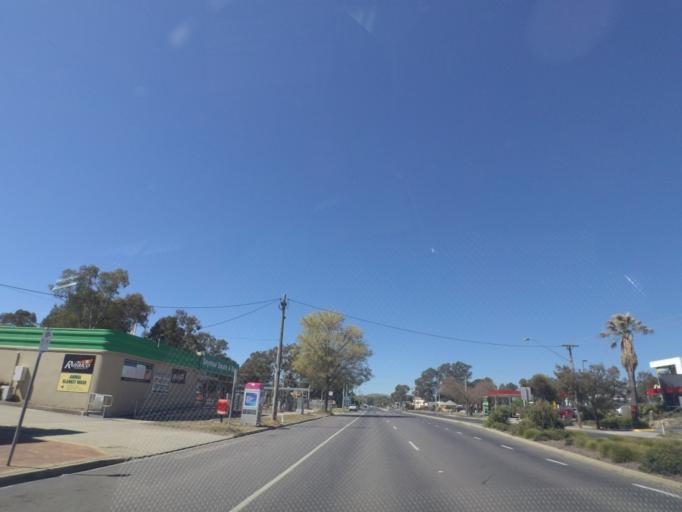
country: AU
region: Victoria
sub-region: Murrindindi
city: Kinglake West
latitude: -37.0199
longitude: 145.1277
